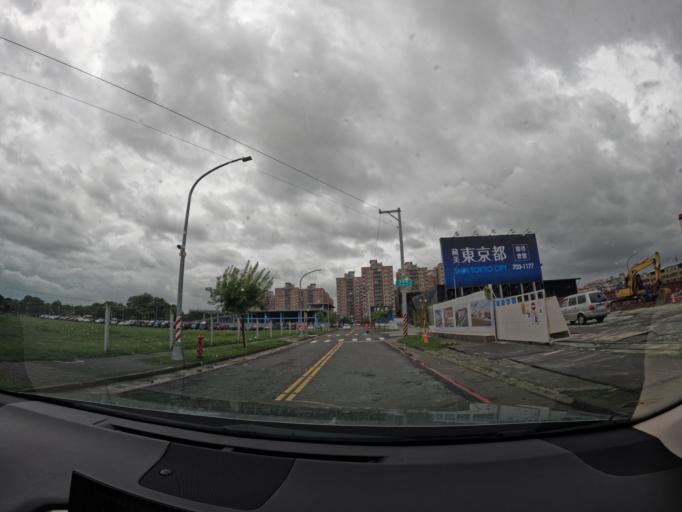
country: TW
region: Taiwan
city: Fengshan
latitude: 22.6332
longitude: 120.3721
